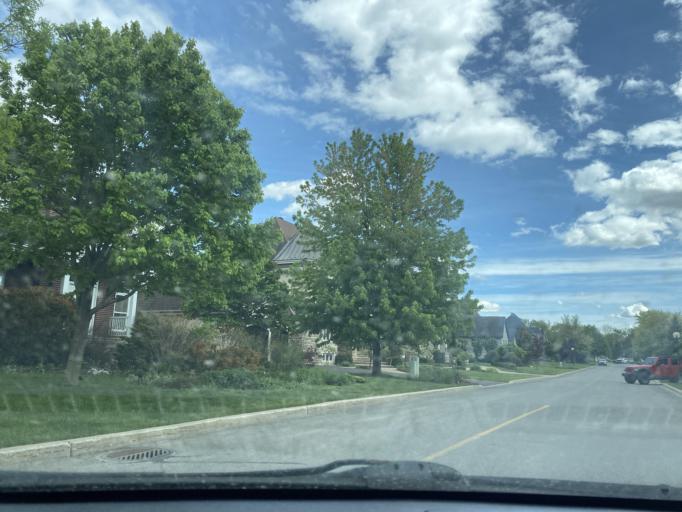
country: CA
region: Quebec
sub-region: Monteregie
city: Chambly
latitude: 45.4736
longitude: -73.2904
